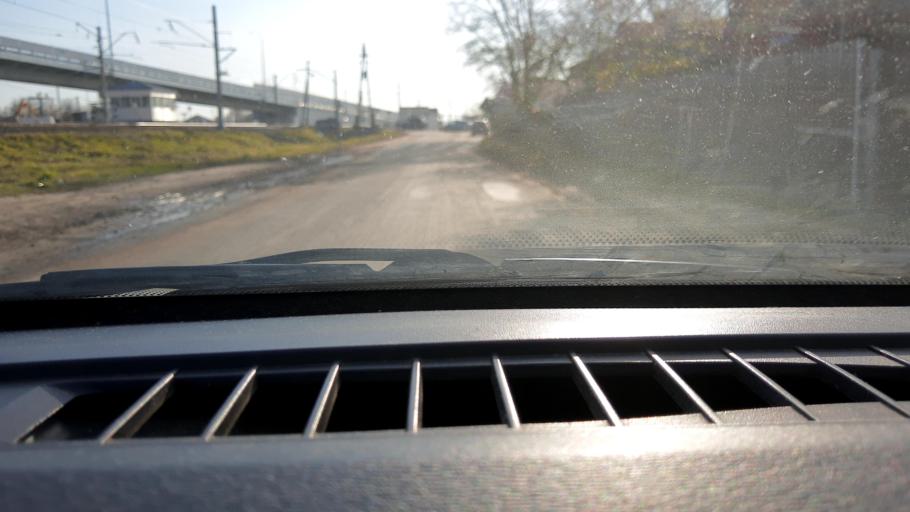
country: RU
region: Nizjnij Novgorod
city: Neklyudovo
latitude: 56.4004
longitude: 43.9811
